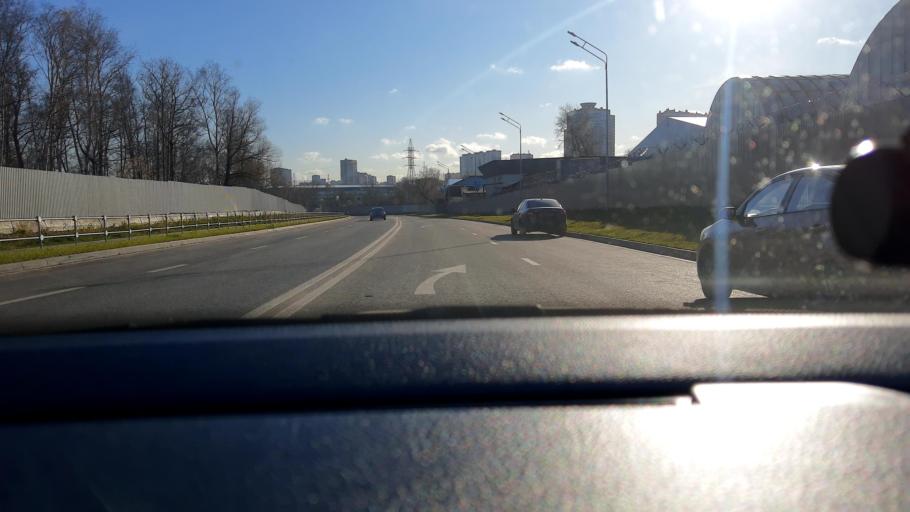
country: RU
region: Moscow
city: Ivanovskoye
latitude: 55.7826
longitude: 37.8469
